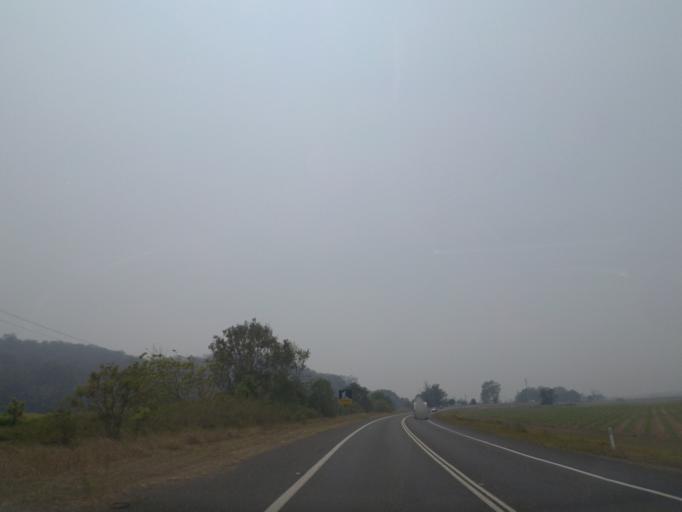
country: AU
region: New South Wales
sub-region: Clarence Valley
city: Maclean
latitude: -29.5415
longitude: 153.1586
